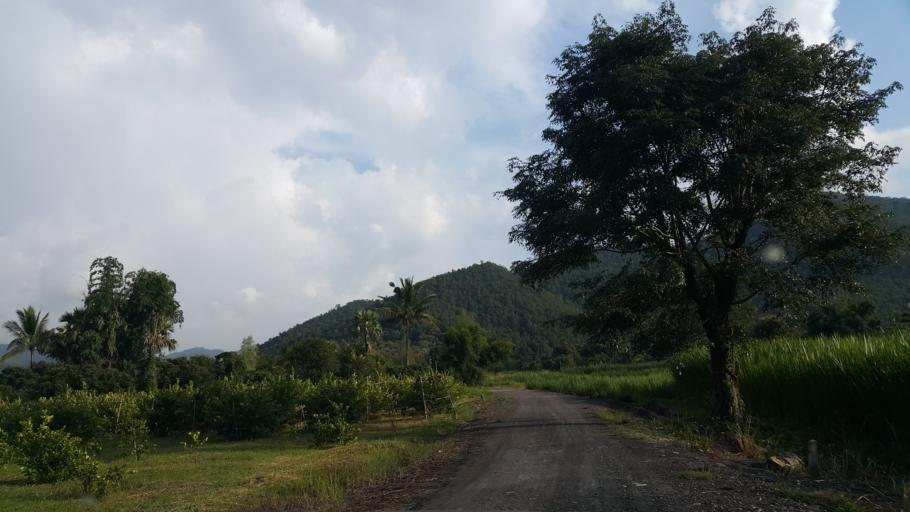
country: TH
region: Chiang Mai
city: Mae On
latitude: 18.7232
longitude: 99.2241
